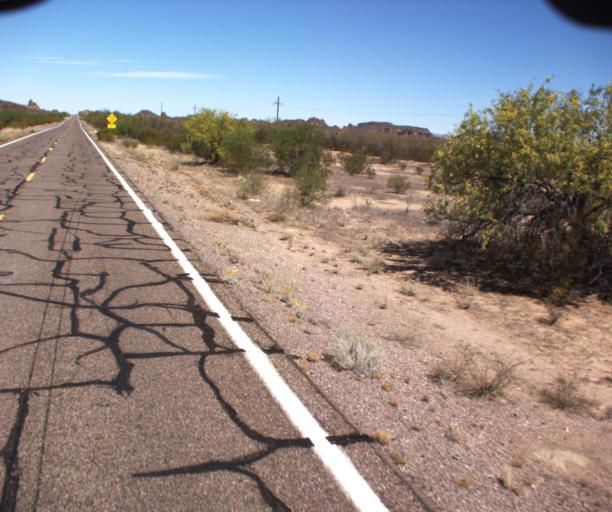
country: US
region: Arizona
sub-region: Pima County
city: Ajo
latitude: 32.5296
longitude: -112.8803
